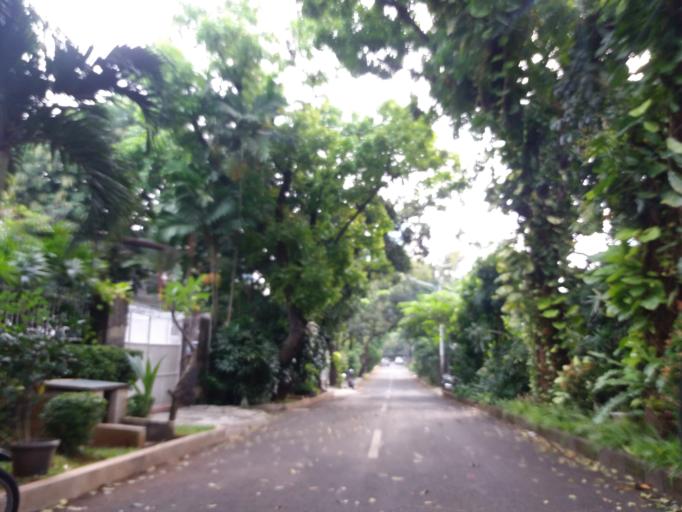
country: ID
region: Jakarta Raya
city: Jakarta
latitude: -6.1979
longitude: 106.8311
